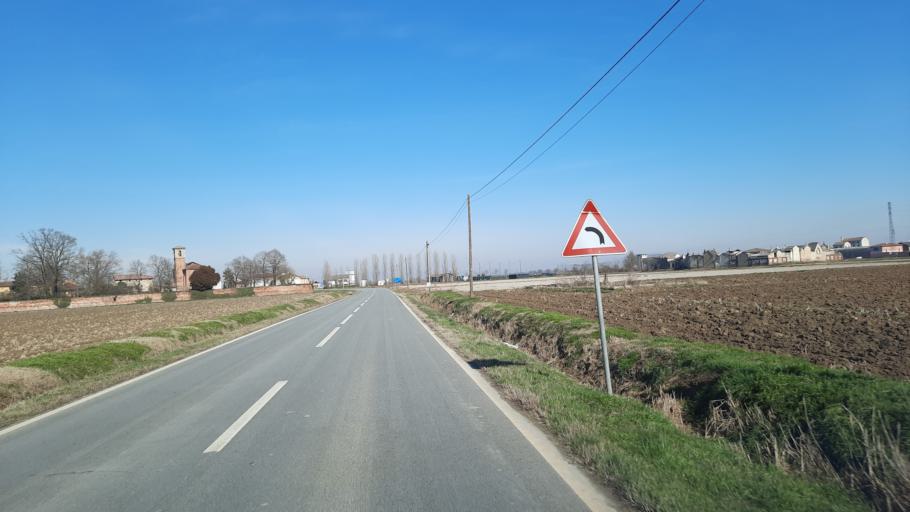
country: IT
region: Piedmont
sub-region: Provincia di Vercelli
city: Pertengo
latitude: 45.2315
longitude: 8.4198
